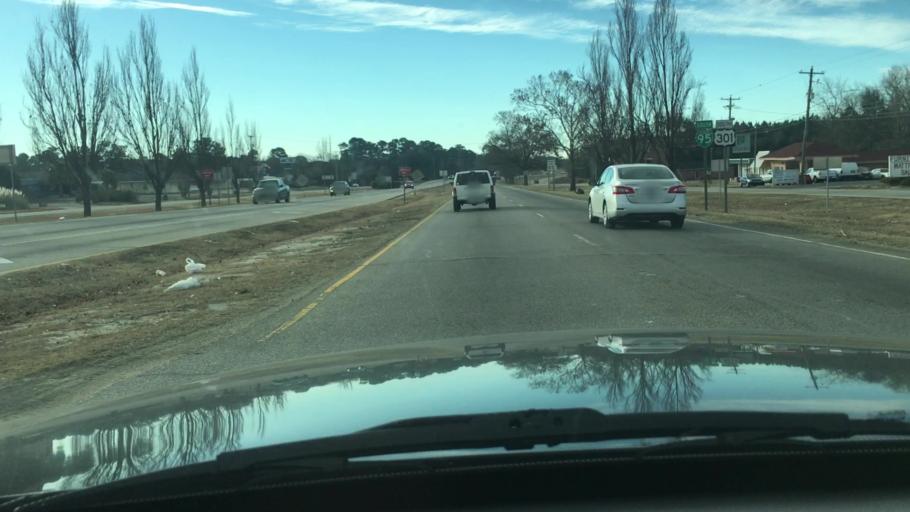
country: US
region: North Carolina
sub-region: Cumberland County
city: Fayetteville
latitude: 35.0129
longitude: -78.8973
